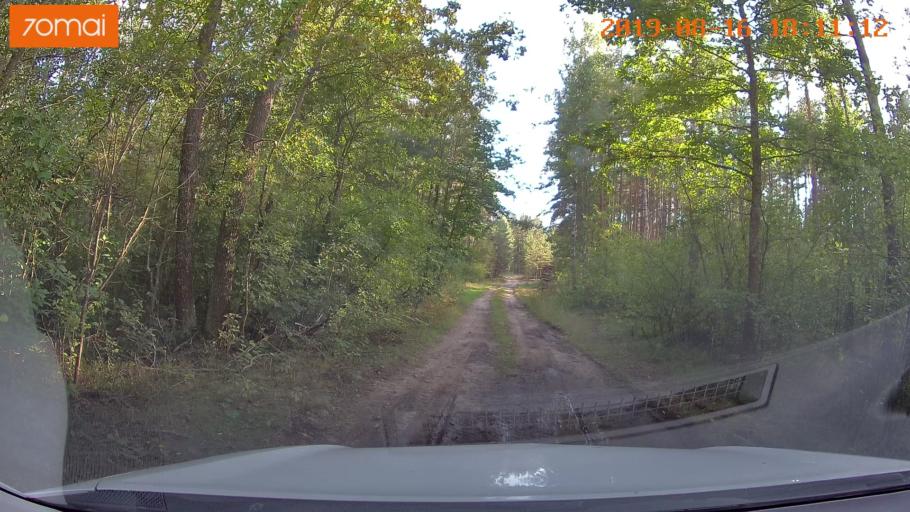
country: BY
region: Mogilev
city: Asipovichy
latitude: 53.2146
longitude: 28.6466
